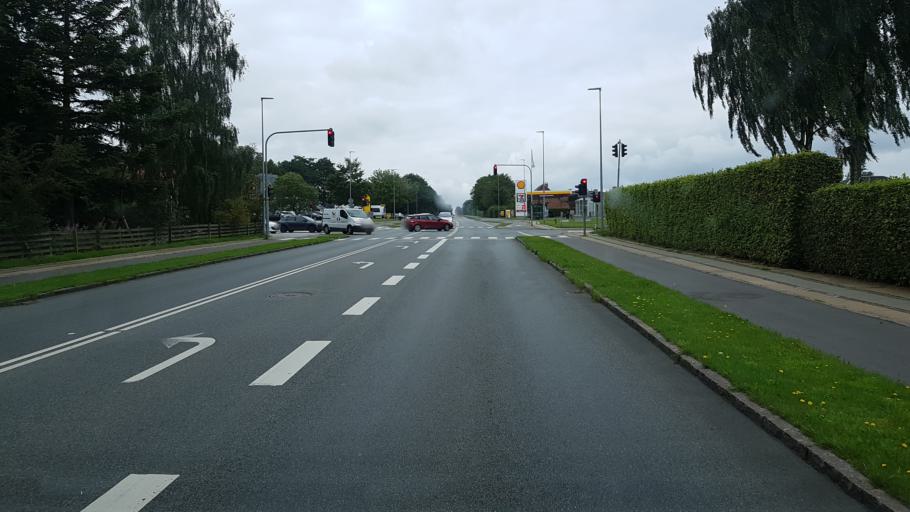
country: DK
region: South Denmark
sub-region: Kolding Kommune
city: Kolding
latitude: 55.4835
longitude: 9.4496
